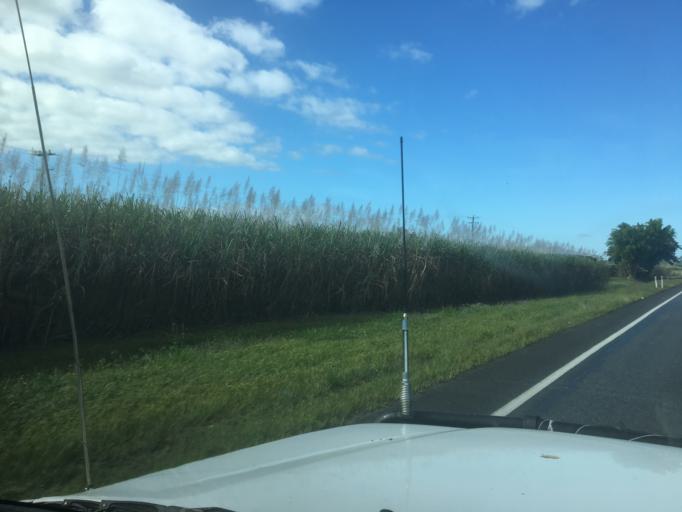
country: AU
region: Queensland
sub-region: Cassowary Coast
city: Innisfail
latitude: -17.3023
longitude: 145.9278
